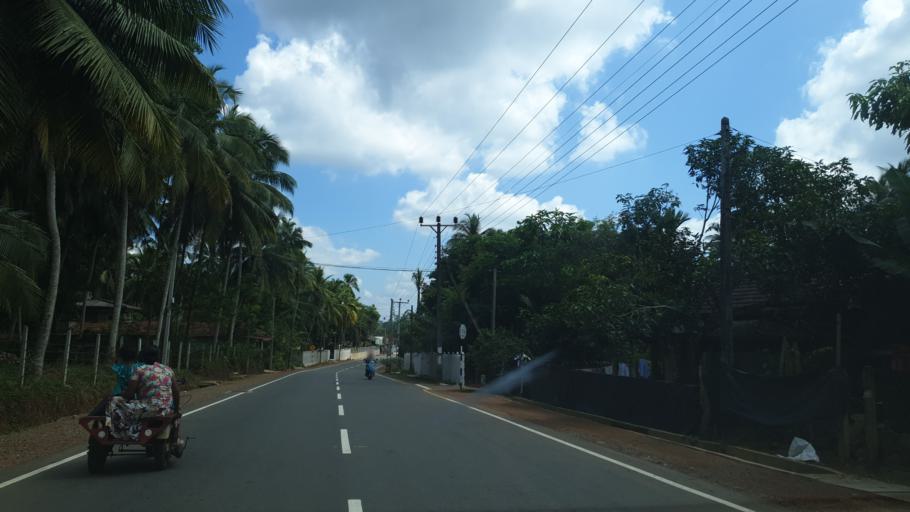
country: LK
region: Western
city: Panadura
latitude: 6.6653
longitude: 79.9545
